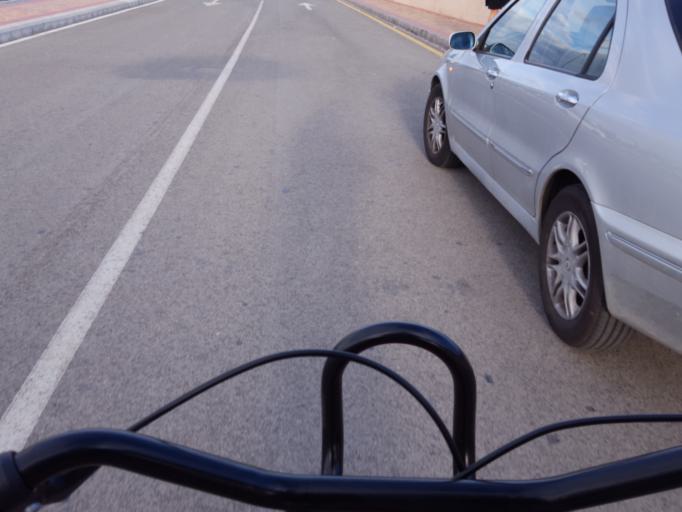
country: ES
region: Murcia
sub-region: Murcia
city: Alcantarilla
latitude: 37.9922
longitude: -1.1853
